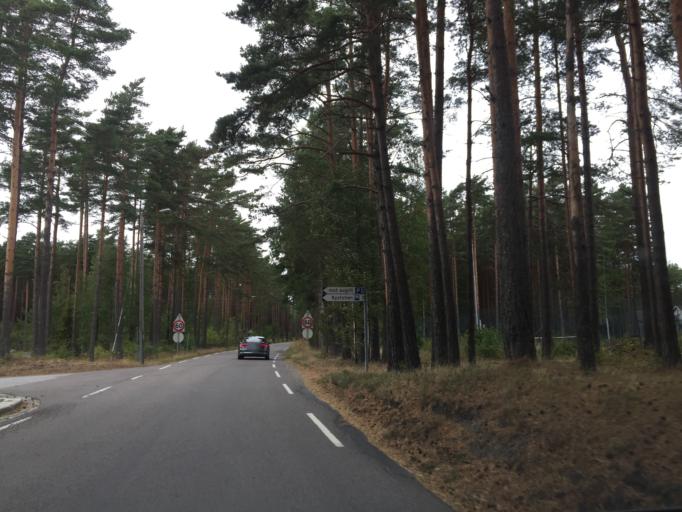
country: NO
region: Ostfold
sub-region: Hvaler
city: Skjaerhalden
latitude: 59.0283
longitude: 11.0314
